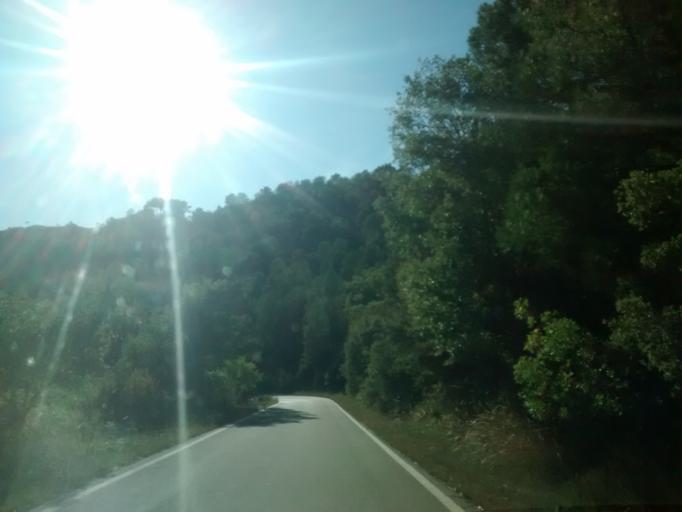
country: ES
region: Aragon
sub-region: Provincia de Huesca
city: Loarre
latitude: 42.3980
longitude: -0.6682
